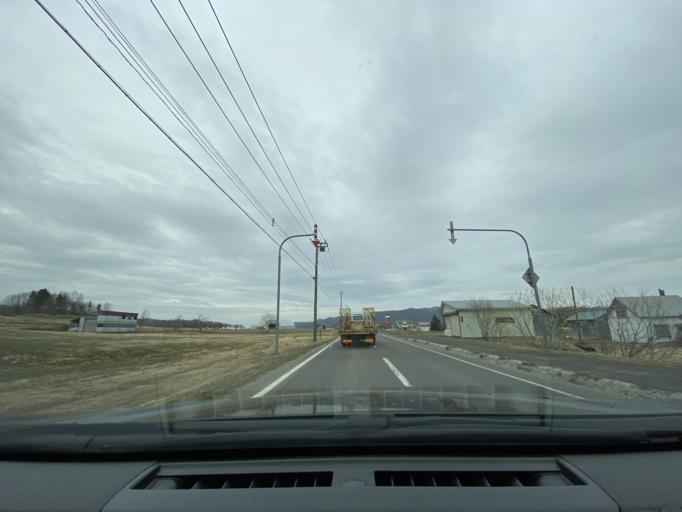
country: JP
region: Hokkaido
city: Nayoro
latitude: 44.1018
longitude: 142.4761
